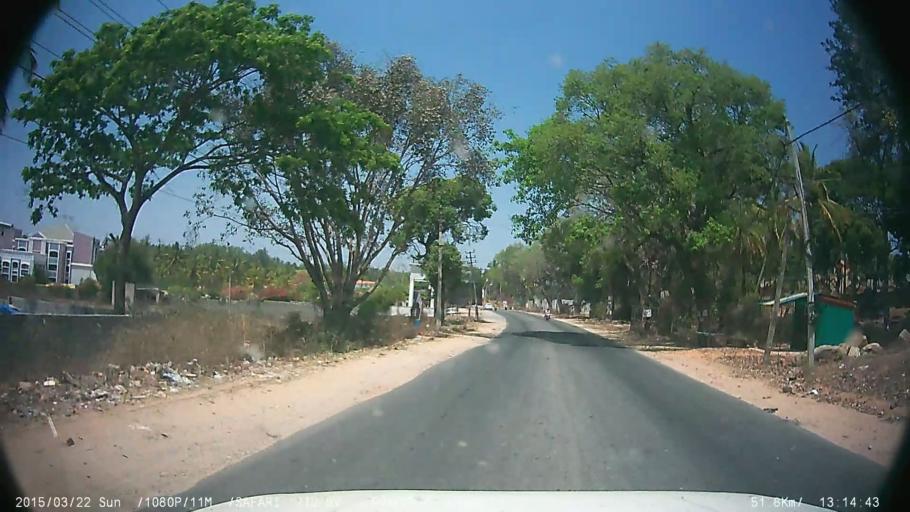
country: IN
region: Karnataka
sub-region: Bangalore Urban
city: Bangalore
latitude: 12.8182
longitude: 77.5841
